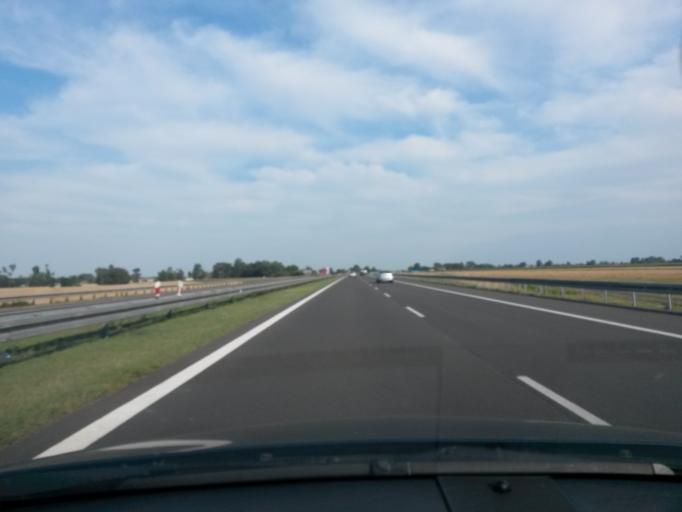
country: PL
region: Greater Poland Voivodeship
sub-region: Powiat slupecki
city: Slupca
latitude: 52.2421
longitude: 17.8727
